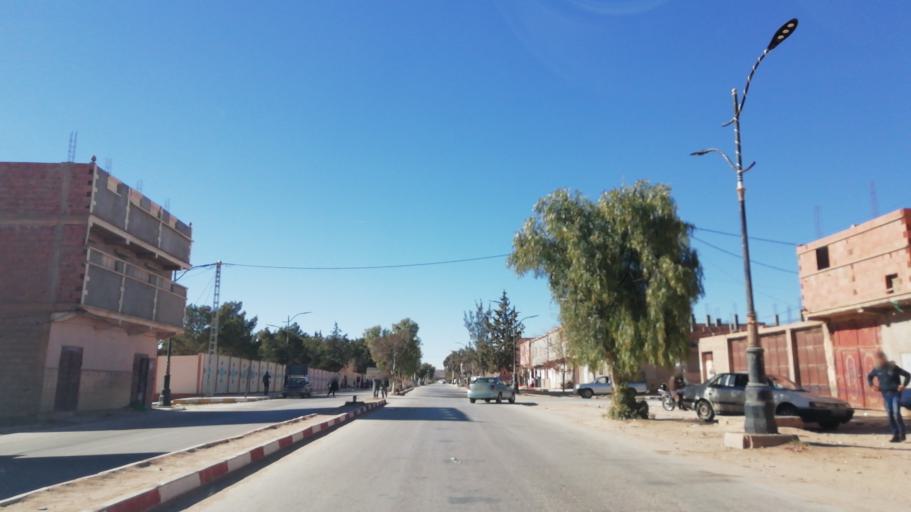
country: DZ
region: El Bayadh
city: El Bayadh
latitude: 33.7276
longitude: 1.5359
